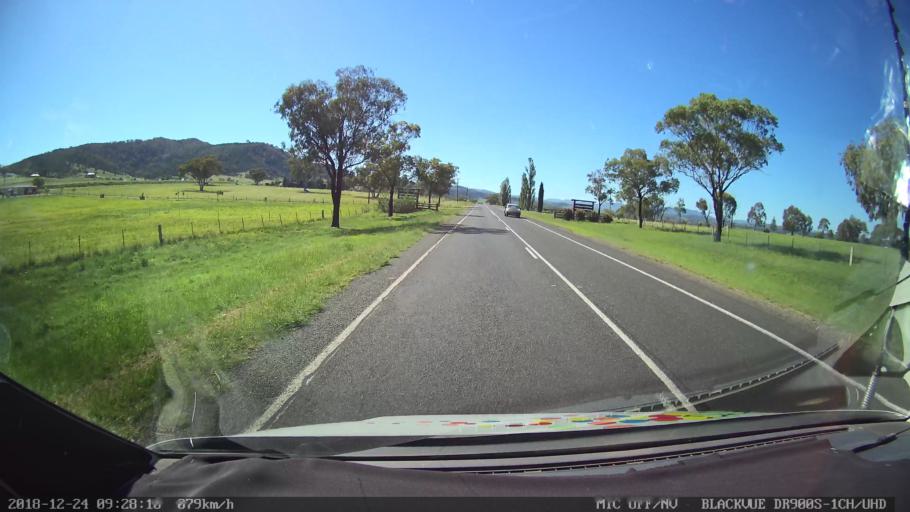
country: AU
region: New South Wales
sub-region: Liverpool Plains
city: Quirindi
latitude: -31.5350
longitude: 150.6865
